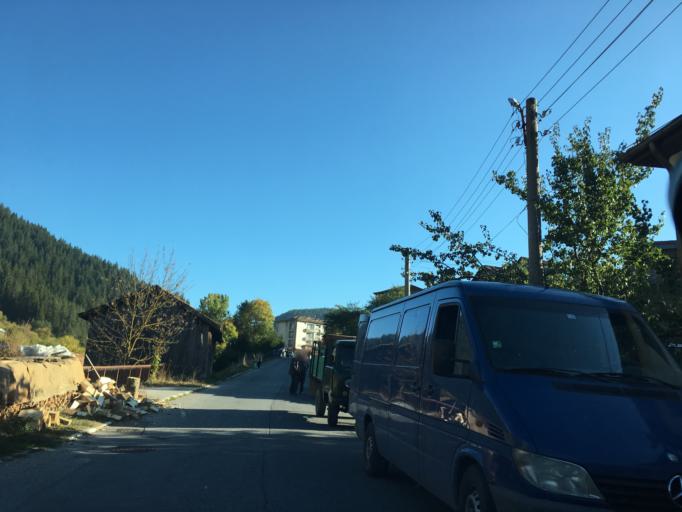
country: BG
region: Smolyan
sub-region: Obshtina Borino
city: Borino
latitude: 41.6008
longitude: 24.3792
